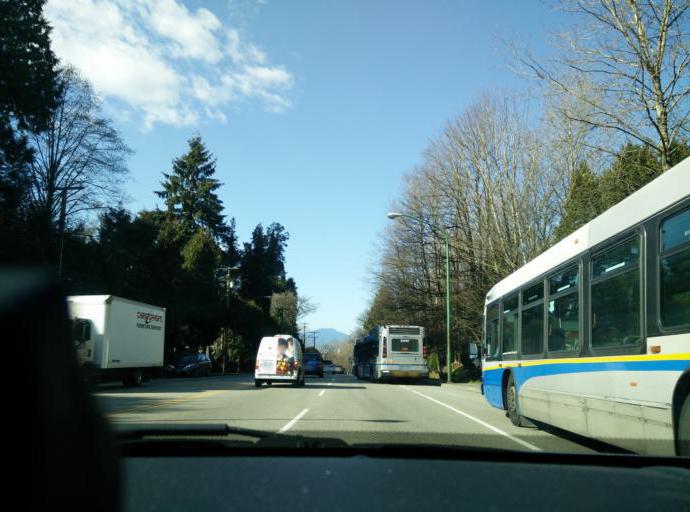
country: CA
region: British Columbia
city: Burnaby
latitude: 49.2361
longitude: -122.9550
